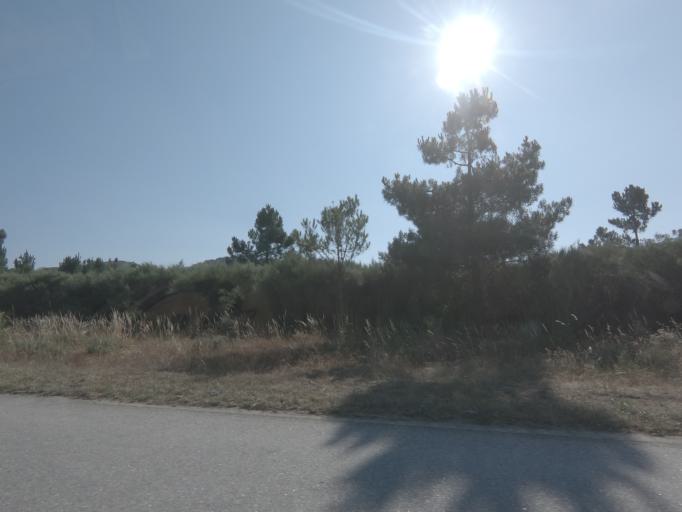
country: PT
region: Viseu
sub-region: Moimenta da Beira
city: Moimenta da Beira
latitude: 41.0355
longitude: -7.5684
